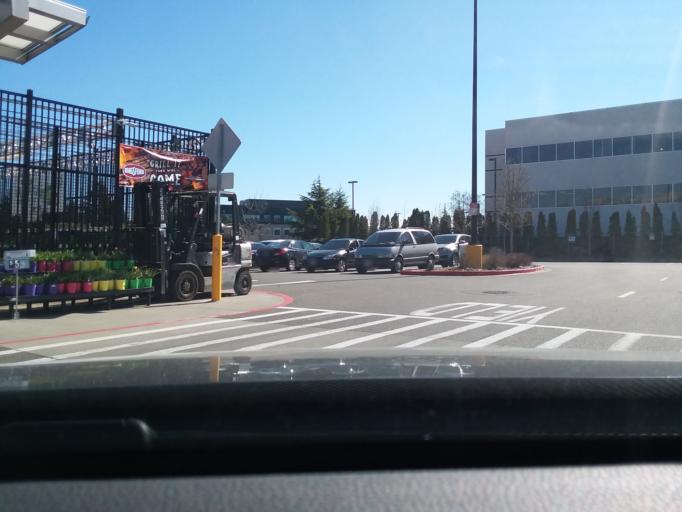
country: US
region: Washington
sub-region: Pierce County
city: Fircrest
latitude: 47.2394
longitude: -122.4795
